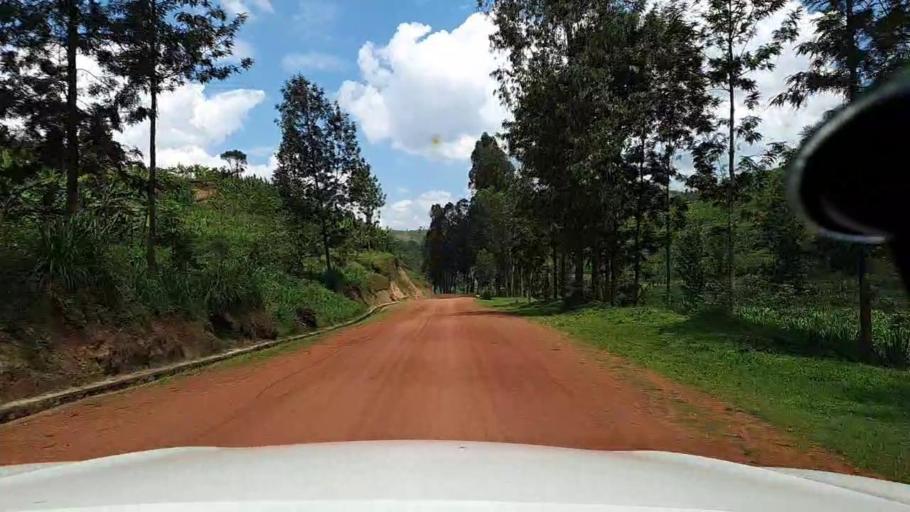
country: RW
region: Northern Province
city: Byumba
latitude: -1.7086
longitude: 29.8491
